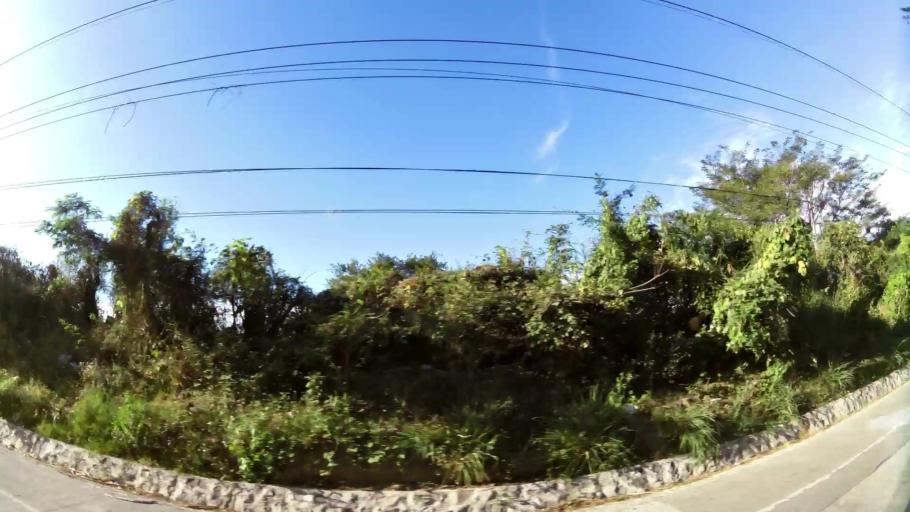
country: SV
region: Santa Ana
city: Metapan
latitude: 14.3029
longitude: -89.4586
